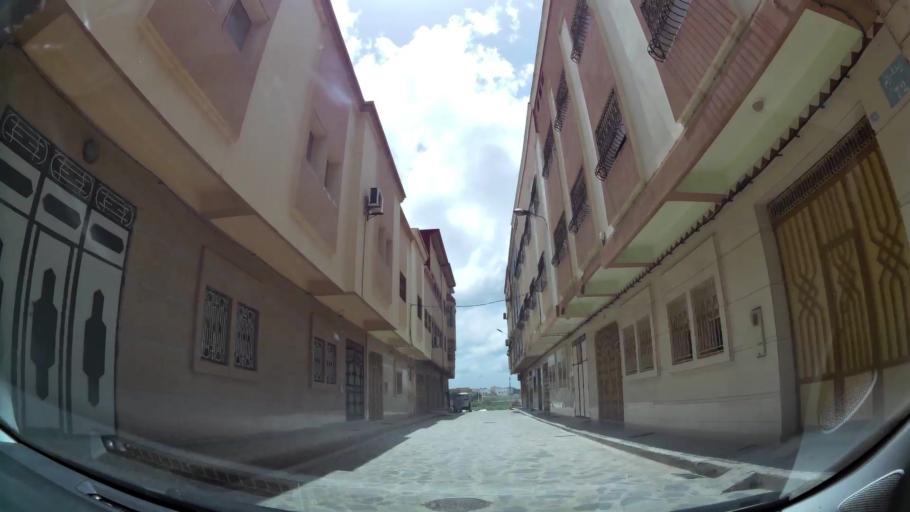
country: MA
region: Oriental
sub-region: Nador
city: Nador
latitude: 35.1660
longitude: -2.9198
